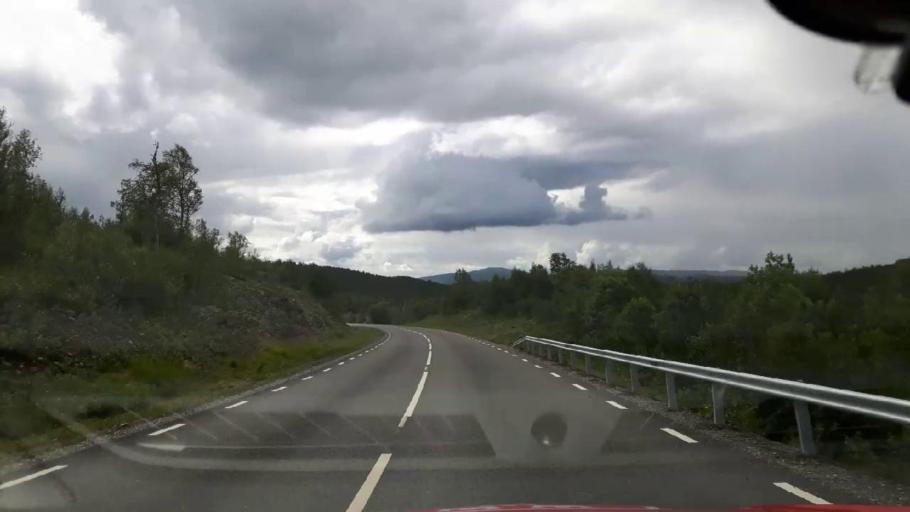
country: NO
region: Nordland
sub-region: Hattfjelldal
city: Hattfjelldal
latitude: 64.9848
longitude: 14.2137
